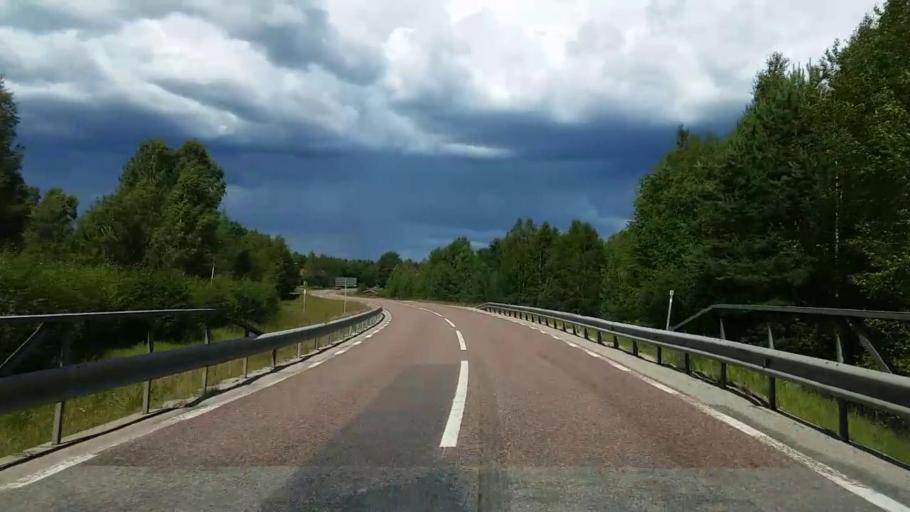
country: SE
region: Gaevleborg
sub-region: Ovanakers Kommun
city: Edsbyn
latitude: 61.3360
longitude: 15.5427
